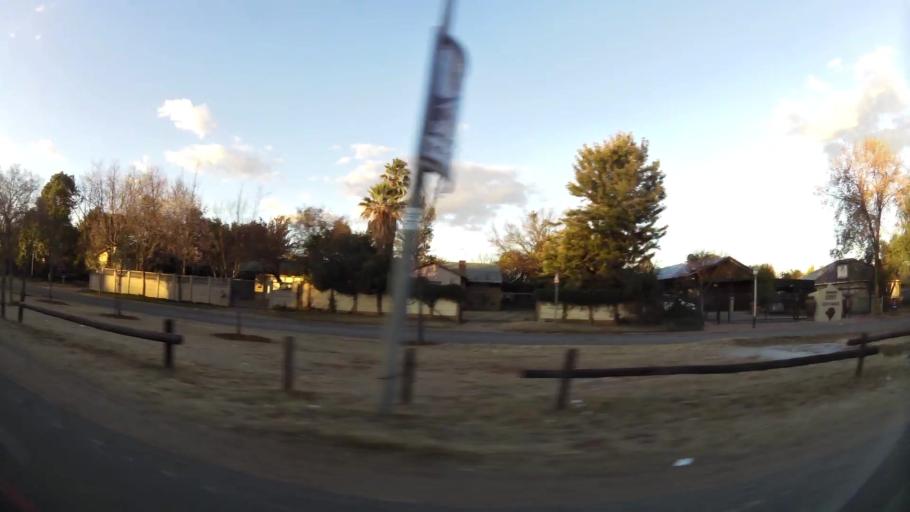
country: ZA
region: North-West
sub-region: Dr Kenneth Kaunda District Municipality
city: Potchefstroom
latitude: -26.7158
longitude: 27.1132
